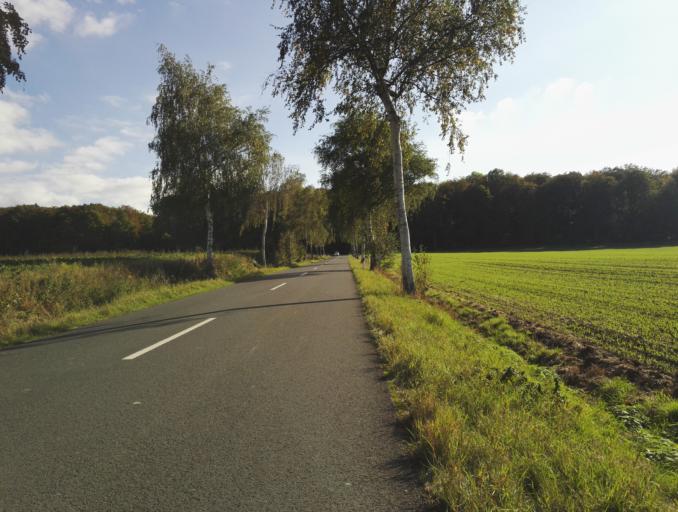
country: DE
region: Lower Saxony
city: Holle
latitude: 52.1393
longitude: 10.1365
